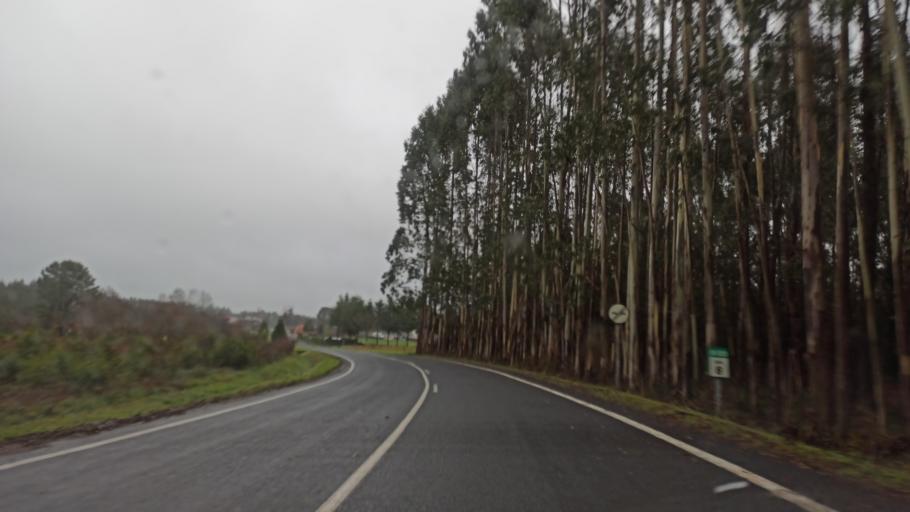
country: ES
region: Galicia
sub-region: Provincia da Coruna
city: Curtis
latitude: 43.1746
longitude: -8.1115
